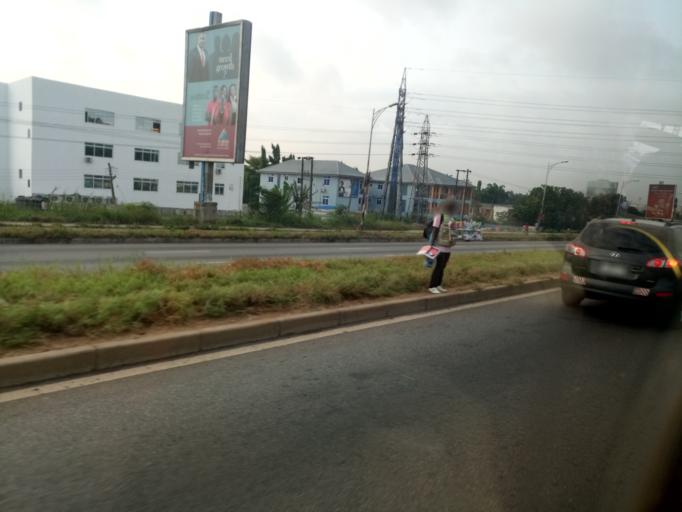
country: GH
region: Greater Accra
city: Medina Estates
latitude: 5.6338
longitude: -0.1772
